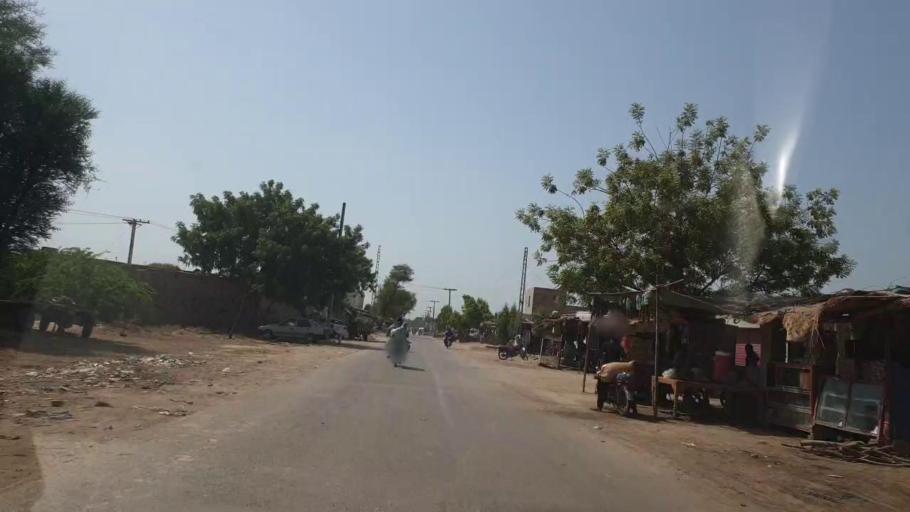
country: PK
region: Sindh
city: Setharja Old
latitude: 27.1294
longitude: 68.5356
